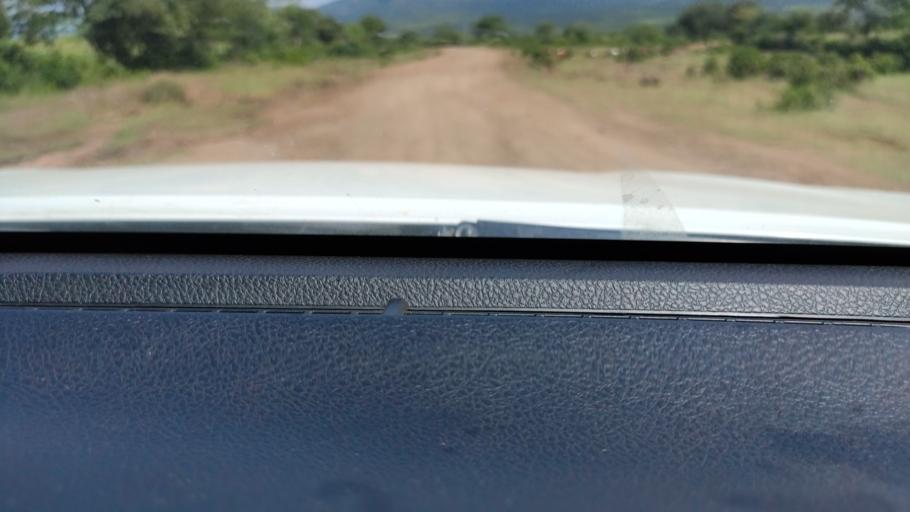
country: ET
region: Southern Nations, Nationalities, and People's Region
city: Felege Neway
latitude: 6.3657
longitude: 36.9826
